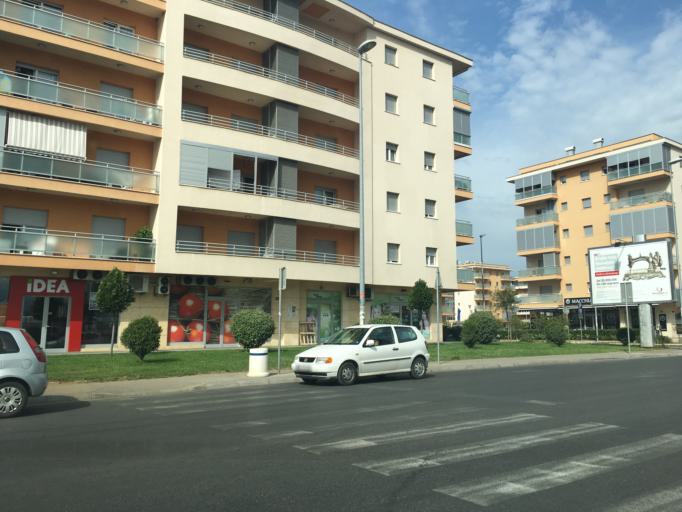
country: ME
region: Podgorica
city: Podgorica
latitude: 42.4395
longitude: 19.2368
